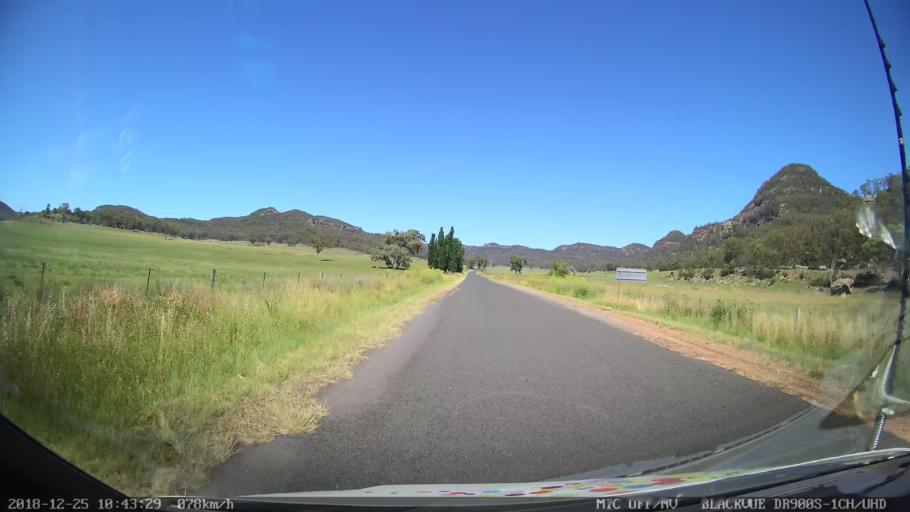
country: AU
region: New South Wales
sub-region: Upper Hunter Shire
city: Merriwa
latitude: -32.4226
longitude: 150.3121
